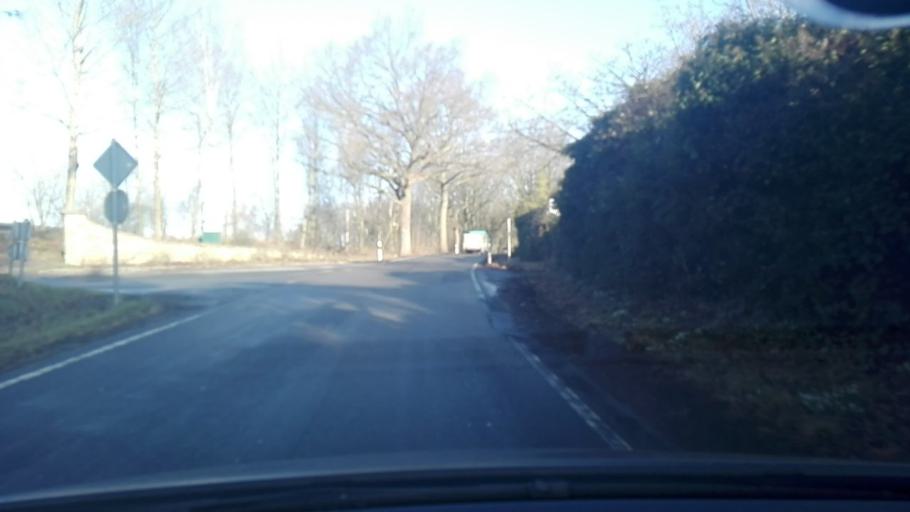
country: DE
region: North Rhine-Westphalia
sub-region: Regierungsbezirk Arnsberg
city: Frondenberg
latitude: 51.4888
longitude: 7.7563
